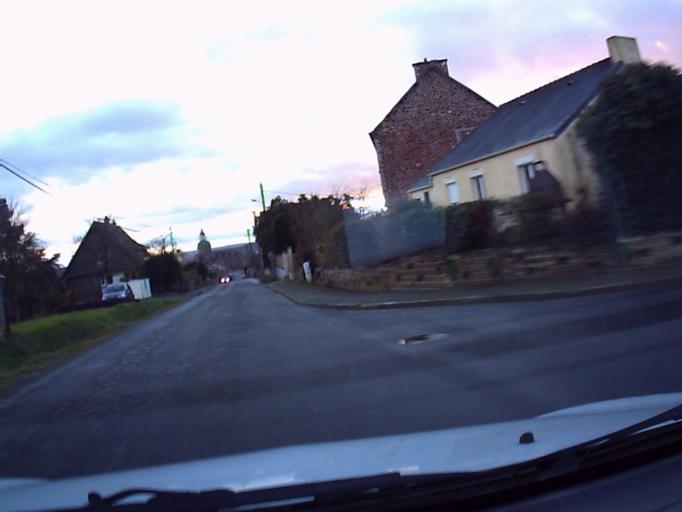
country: FR
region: Brittany
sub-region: Departement d'Ille-et-Vilaine
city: Iffendic
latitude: 48.1323
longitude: -2.0311
